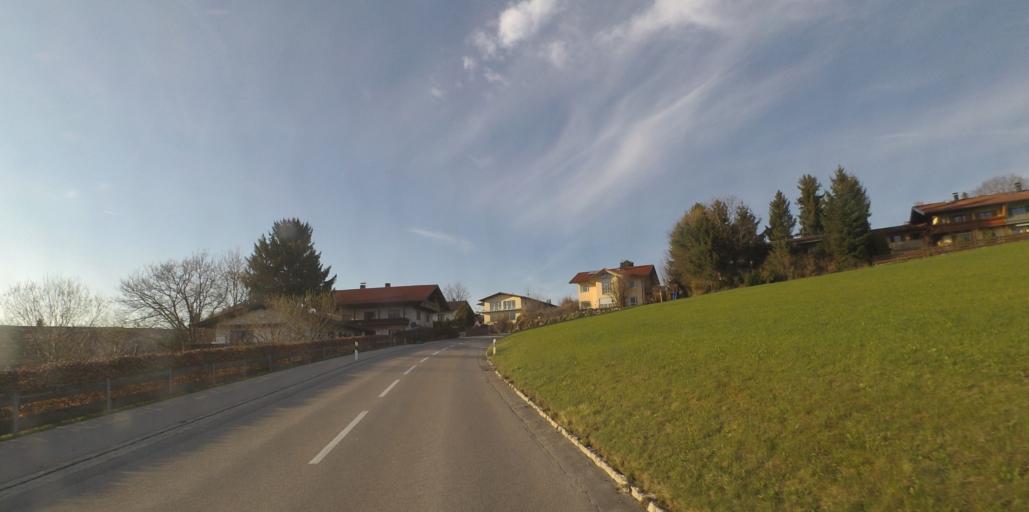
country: DE
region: Bavaria
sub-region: Upper Bavaria
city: Bergen
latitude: 47.8218
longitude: 12.5936
